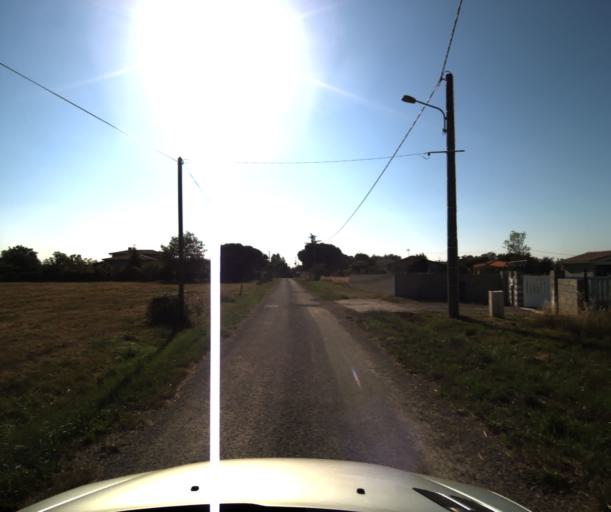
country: FR
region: Midi-Pyrenees
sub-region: Departement de la Haute-Garonne
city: Saubens
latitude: 43.4739
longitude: 1.3673
